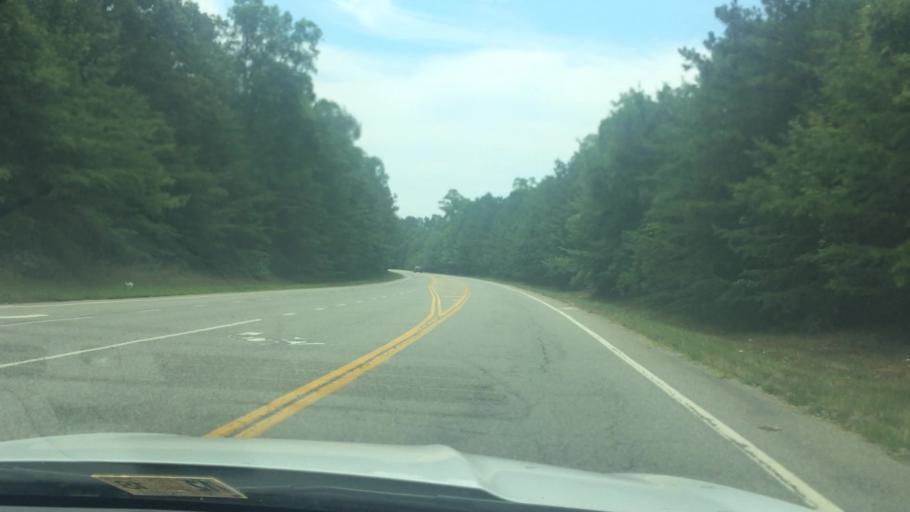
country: US
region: Virginia
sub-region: James City County
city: Williamsburg
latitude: 37.2720
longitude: -76.8081
